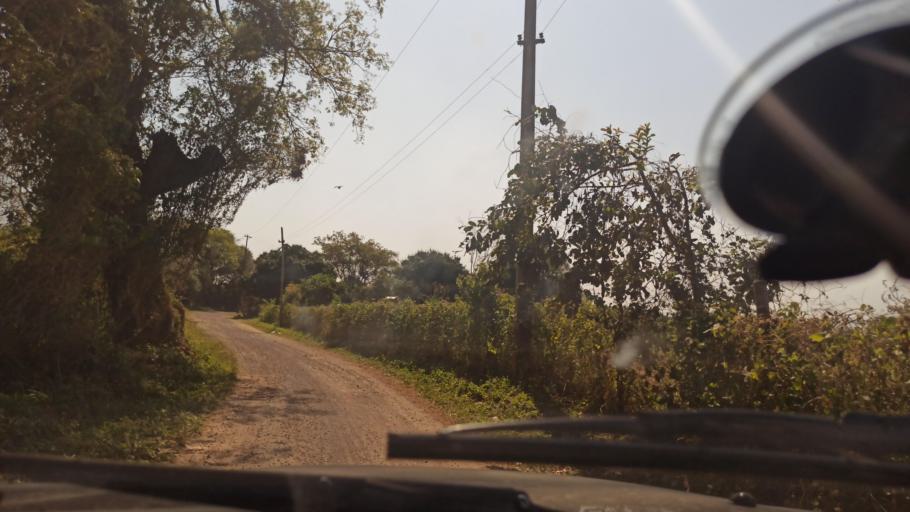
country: AR
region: Formosa
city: Clorinda
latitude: -25.3244
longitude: -57.6920
